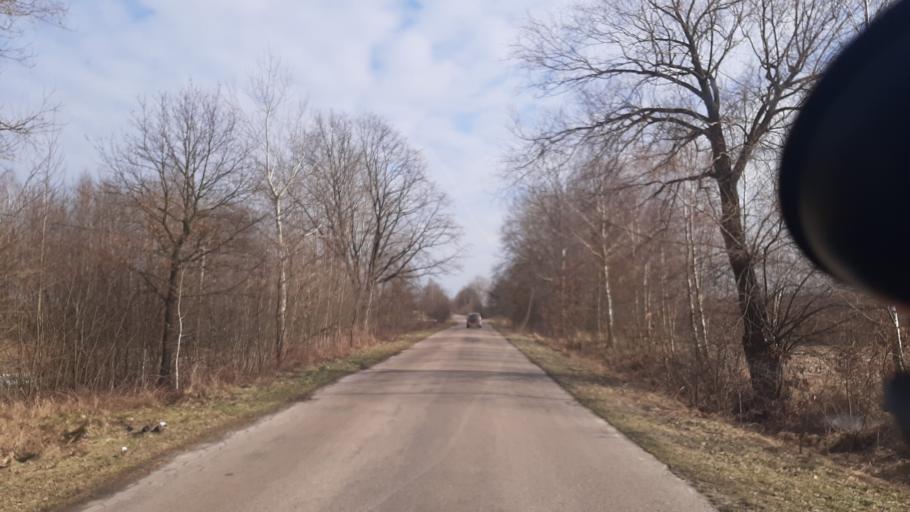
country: PL
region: Lublin Voivodeship
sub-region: Powiat lubartowski
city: Uscimow Stary
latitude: 51.4691
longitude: 22.9774
